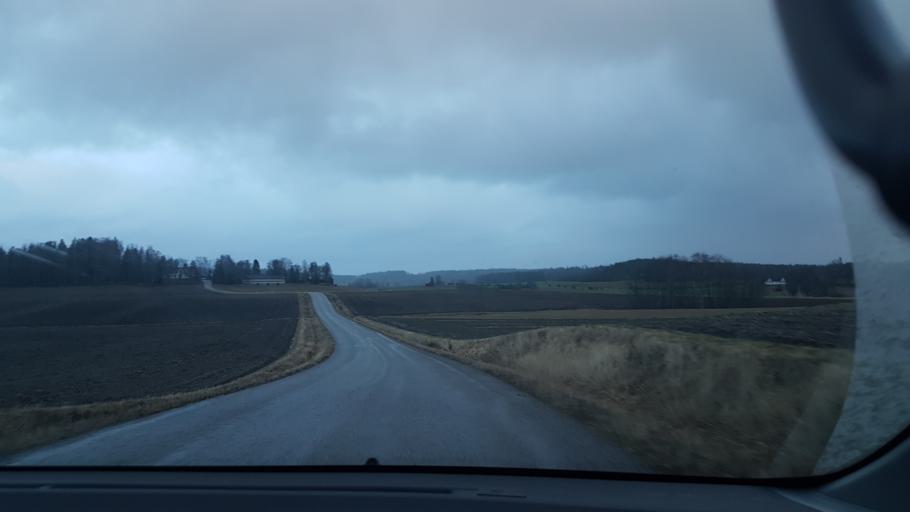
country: FI
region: Uusimaa
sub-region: Helsinki
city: Lohja
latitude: 60.2063
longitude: 24.0992
